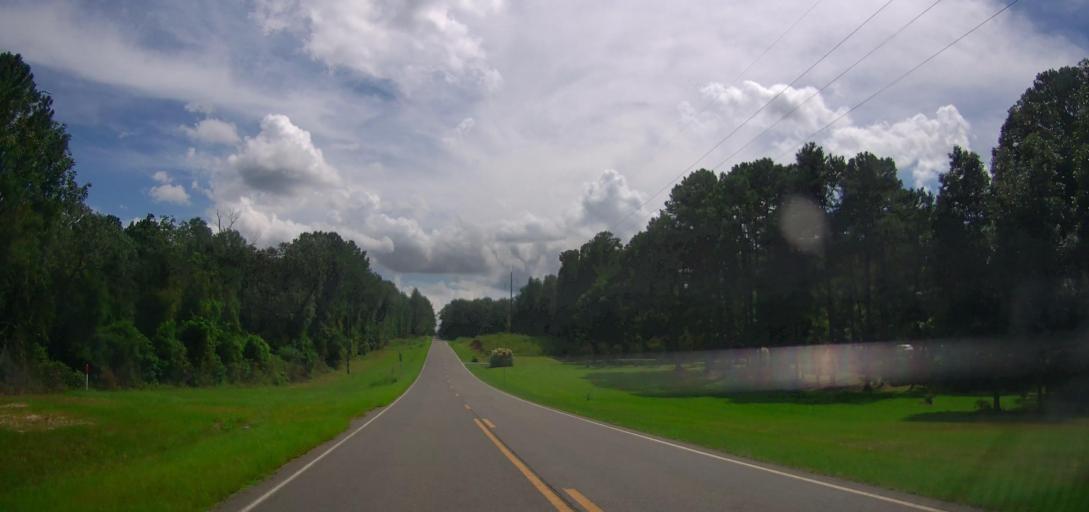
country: US
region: Georgia
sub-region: Taylor County
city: Butler
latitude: 32.5124
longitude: -84.2044
